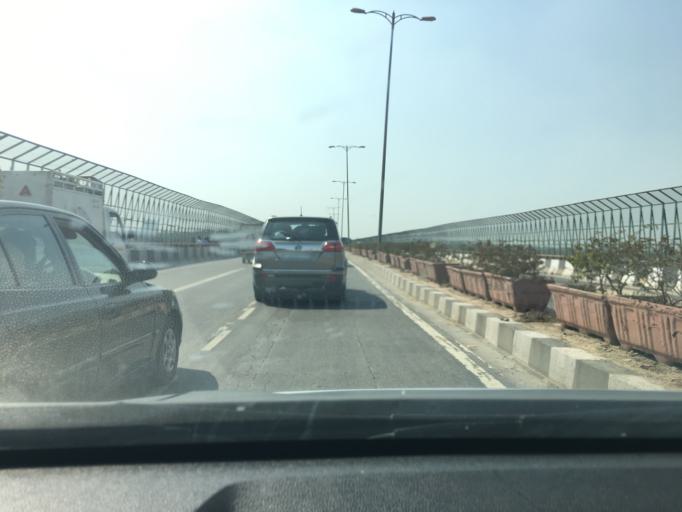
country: IN
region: NCT
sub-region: North Delhi
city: Delhi
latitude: 28.6515
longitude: 77.2647
